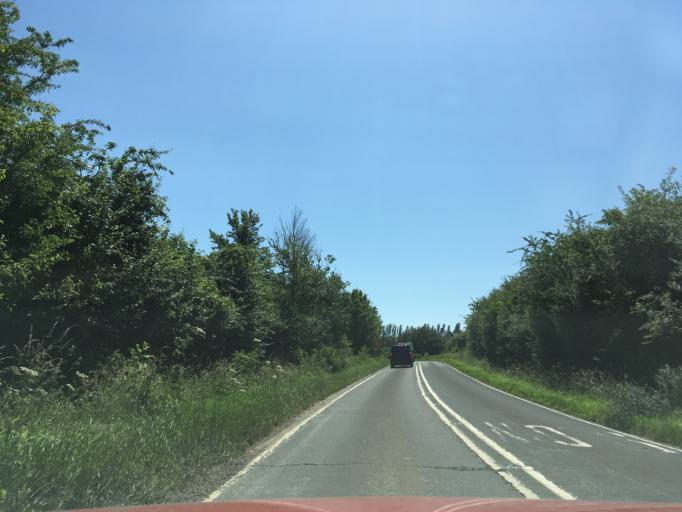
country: GB
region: England
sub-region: Northamptonshire
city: Brackley
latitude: 51.9973
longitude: -1.1802
